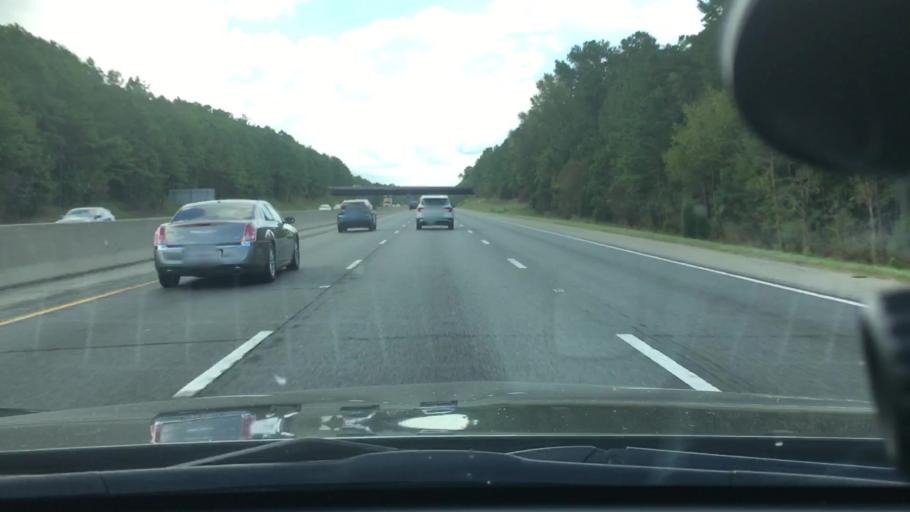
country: US
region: North Carolina
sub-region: Orange County
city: Chapel Hill
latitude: 35.9361
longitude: -78.9903
